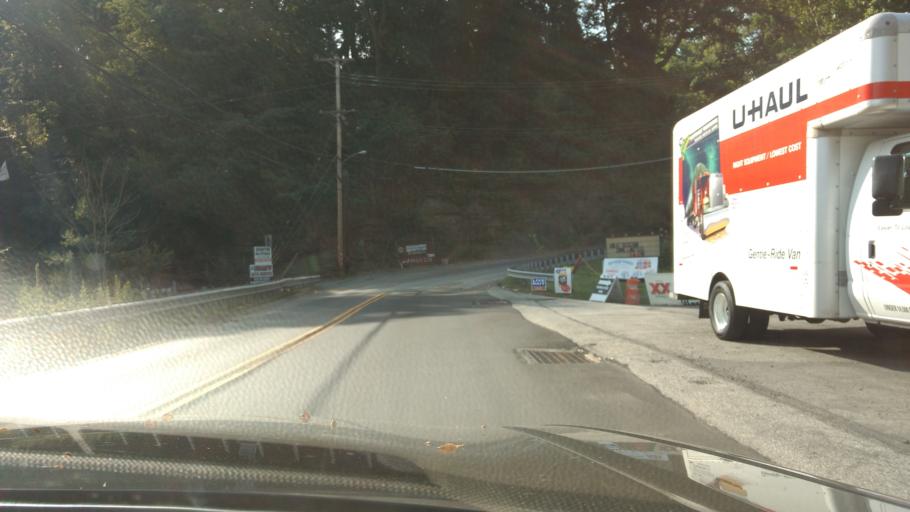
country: US
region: Pennsylvania
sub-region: Allegheny County
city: Bellevue
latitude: 40.4900
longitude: -80.0452
